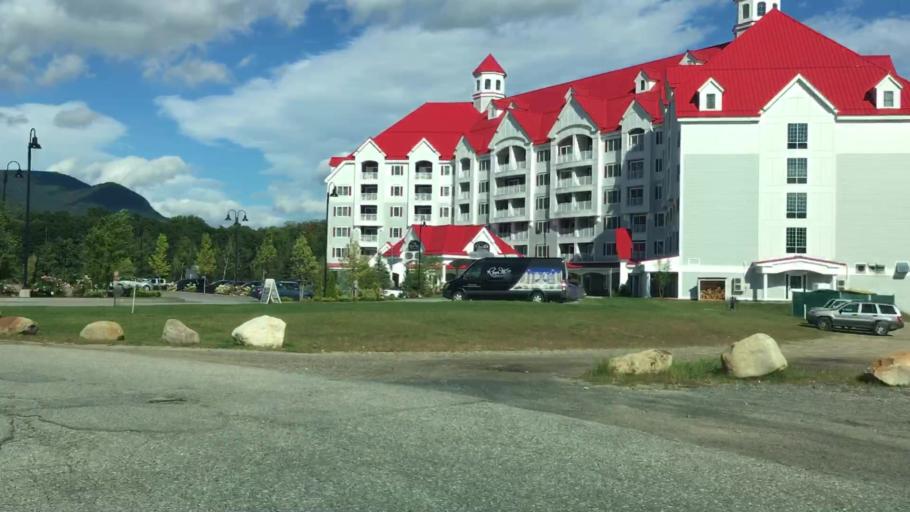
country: US
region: New Hampshire
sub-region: Grafton County
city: Woodstock
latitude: 44.0418
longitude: -71.6692
